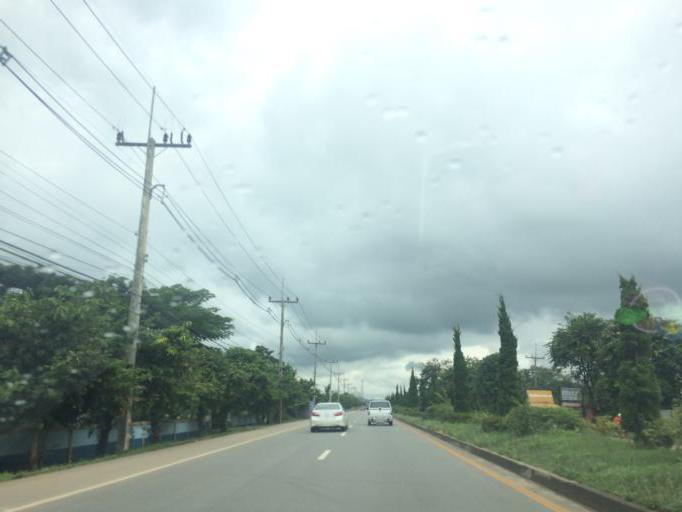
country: TH
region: Chiang Rai
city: Mae Chan
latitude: 20.0331
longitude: 99.8743
